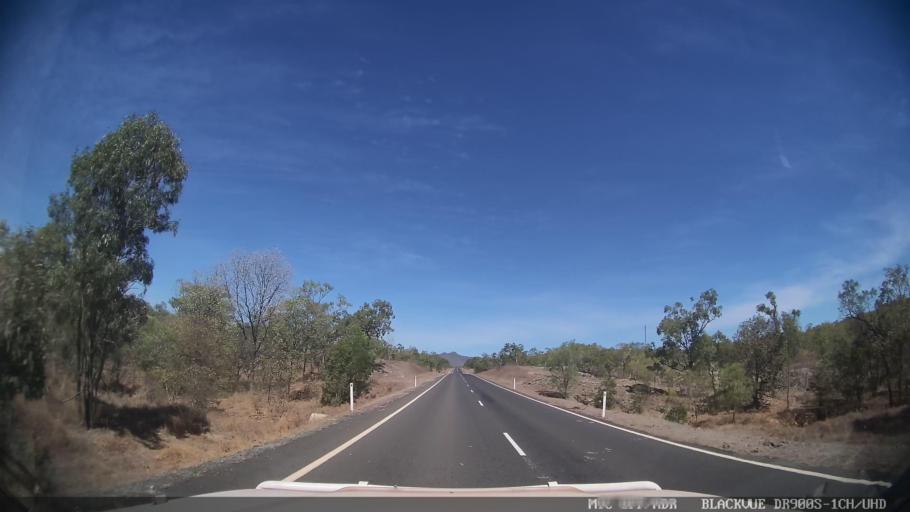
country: AU
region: Queensland
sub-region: Cook
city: Cooktown
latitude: -15.7003
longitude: 144.6058
